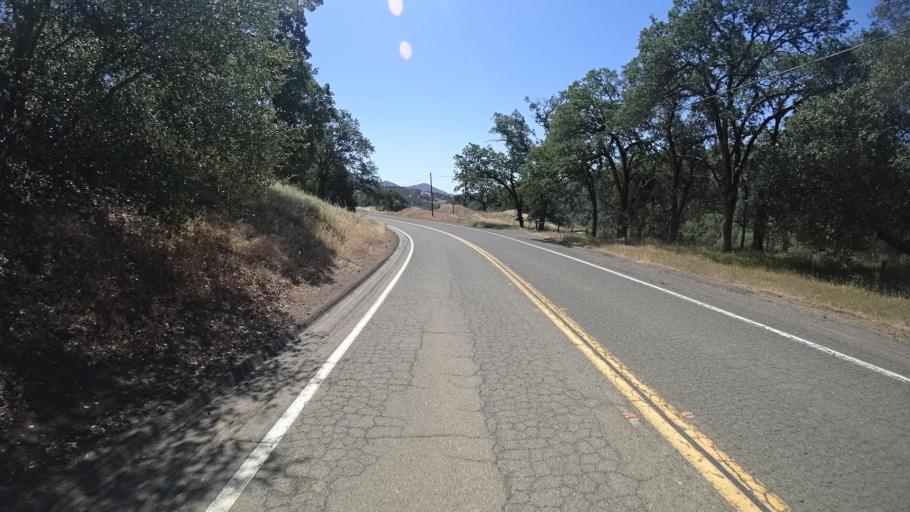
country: US
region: California
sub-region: Lake County
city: Lower Lake
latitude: 38.8904
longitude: -122.5400
